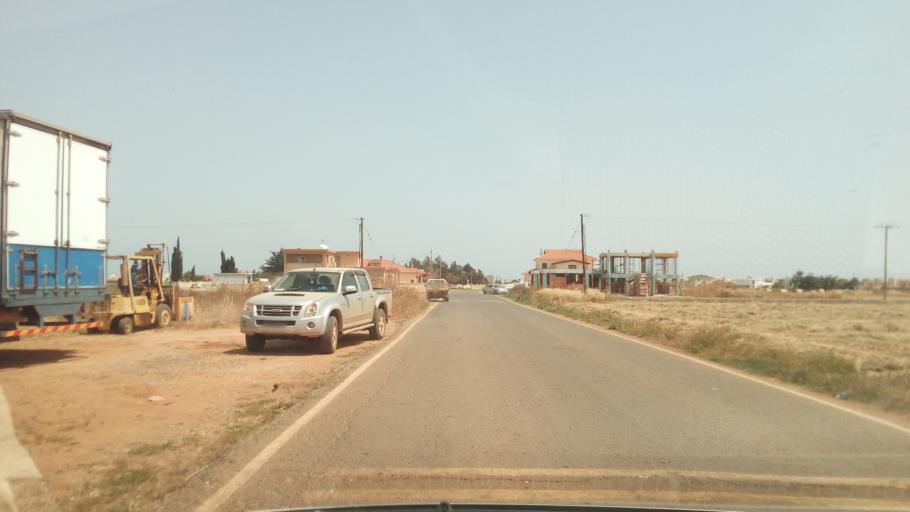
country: CY
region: Ammochostos
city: Avgorou
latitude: 34.9811
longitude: 33.8416
